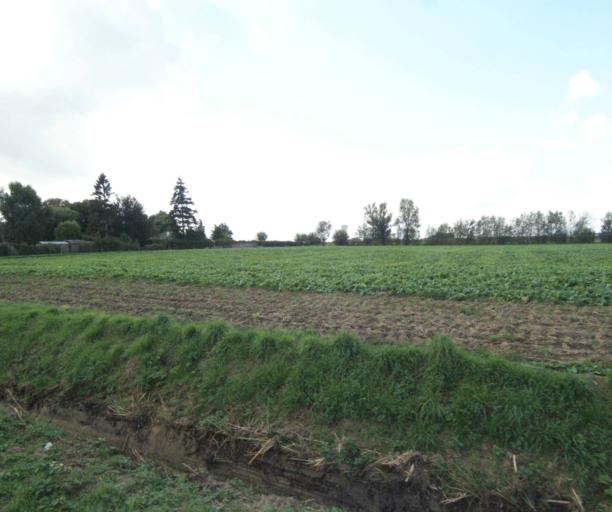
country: FR
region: Nord-Pas-de-Calais
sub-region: Departement du Nord
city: Herlies
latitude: 50.5847
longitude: 2.8415
